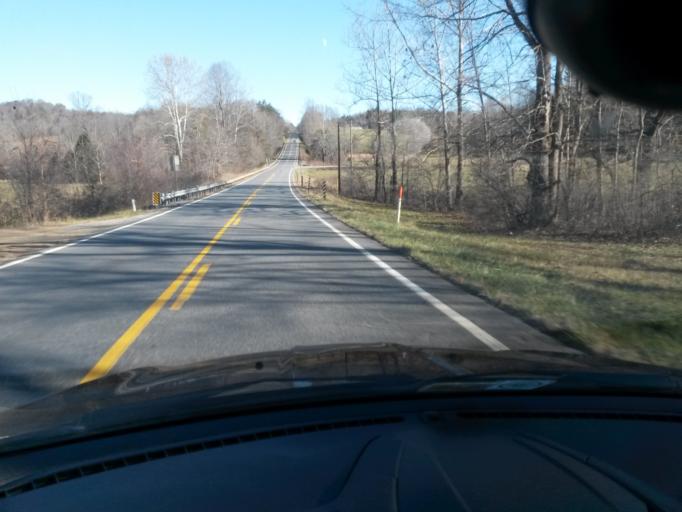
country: US
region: Virginia
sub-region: Patrick County
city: Patrick Springs
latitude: 36.7445
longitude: -80.2057
